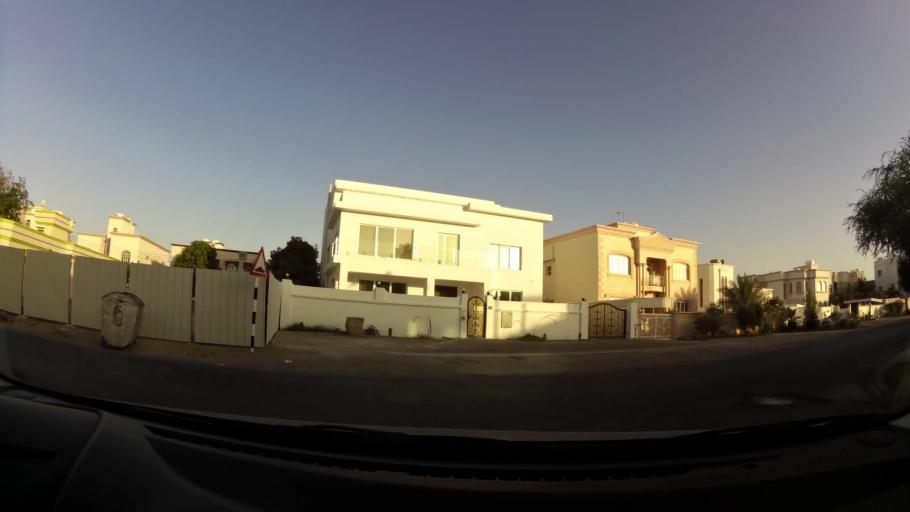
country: OM
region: Muhafazat Masqat
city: As Sib al Jadidah
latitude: 23.5996
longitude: 58.2246
